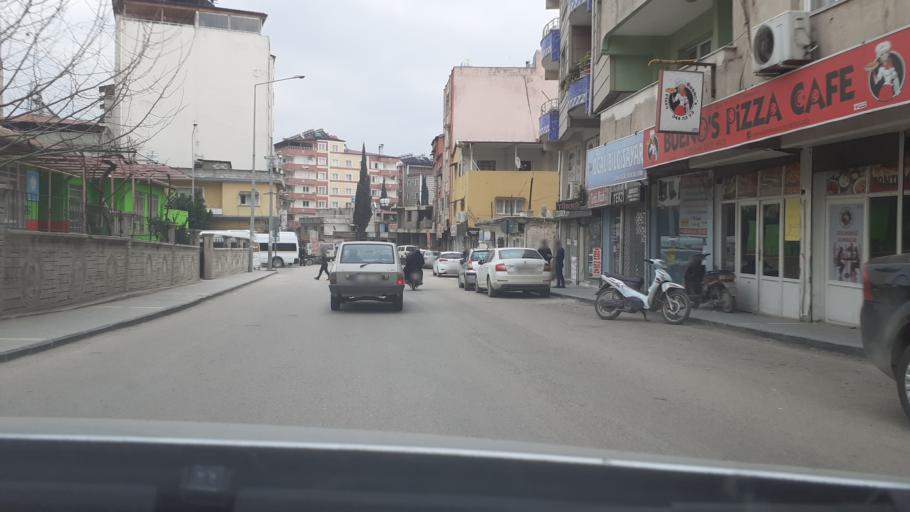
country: TR
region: Hatay
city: Kirikhan
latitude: 36.4971
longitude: 36.3572
